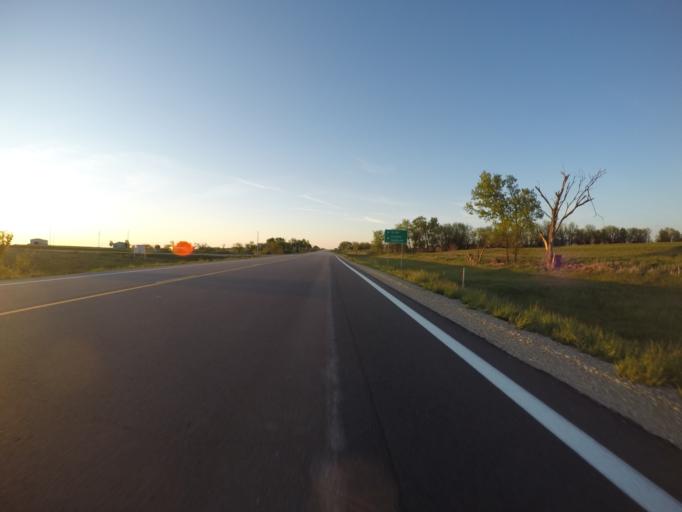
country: US
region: Kansas
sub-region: Pottawatomie County
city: Westmoreland
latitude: 39.4276
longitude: -96.5199
